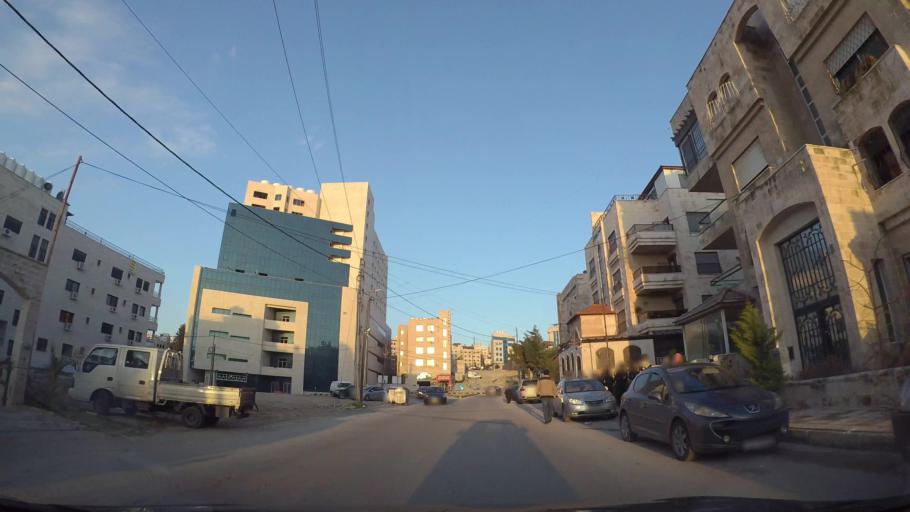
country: JO
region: Amman
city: Al Jubayhah
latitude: 31.9990
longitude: 35.8771
